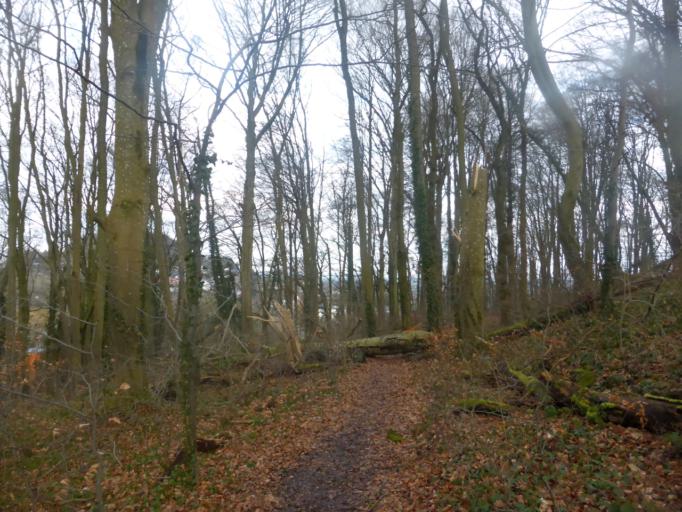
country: LU
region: Luxembourg
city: Belvaux
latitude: 49.5203
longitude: 5.9326
